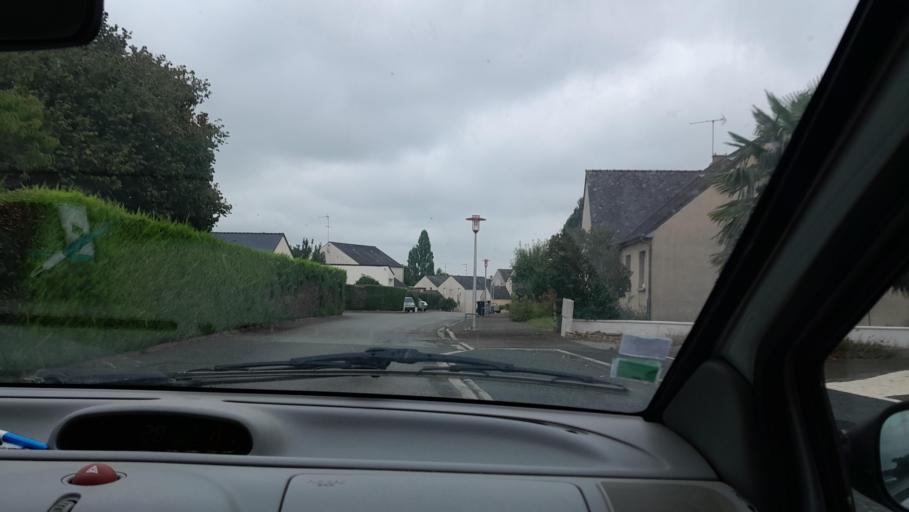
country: FR
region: Pays de la Loire
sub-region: Departement de la Mayenne
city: Cosse-le-Vivien
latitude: 47.9497
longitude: -0.9144
